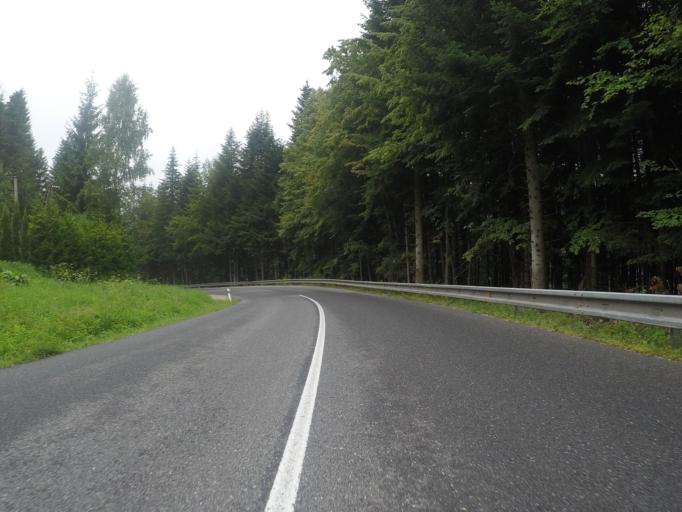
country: SK
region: Kosicky
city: Spisska Nova Ves
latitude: 48.8745
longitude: 20.5259
